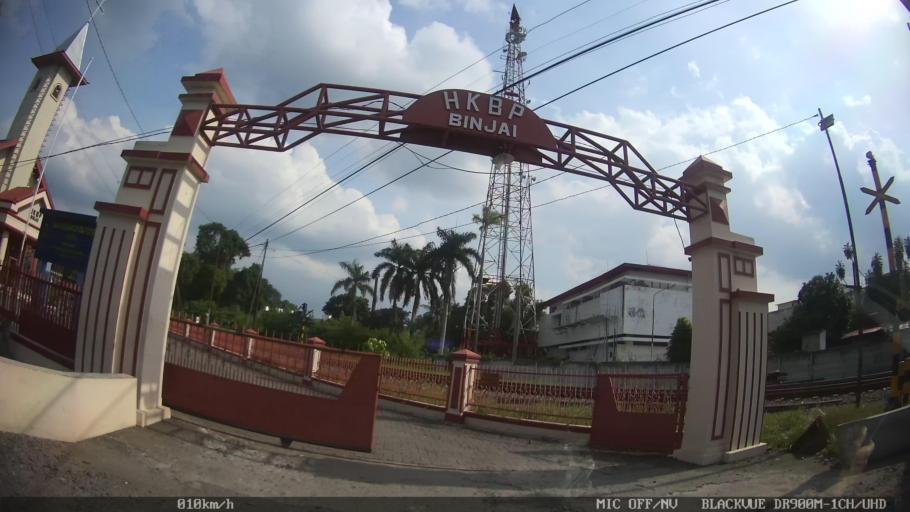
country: ID
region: North Sumatra
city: Binjai
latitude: 3.6106
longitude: 98.4963
